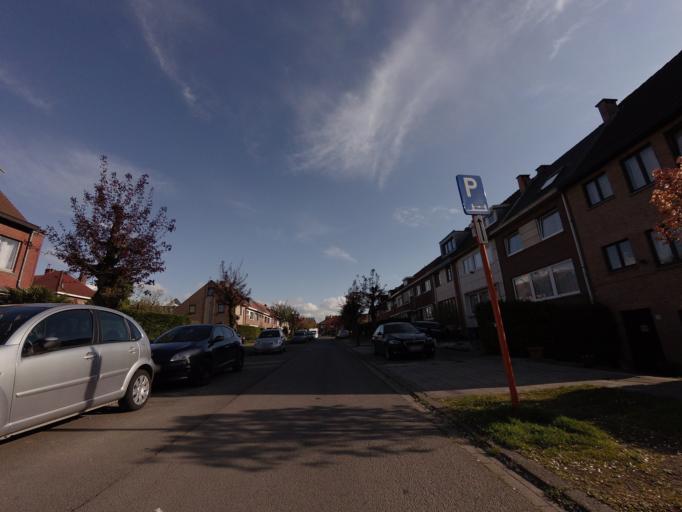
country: BE
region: Flanders
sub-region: Provincie Vlaams-Brabant
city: Grimbergen
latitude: 50.9143
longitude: 4.3705
